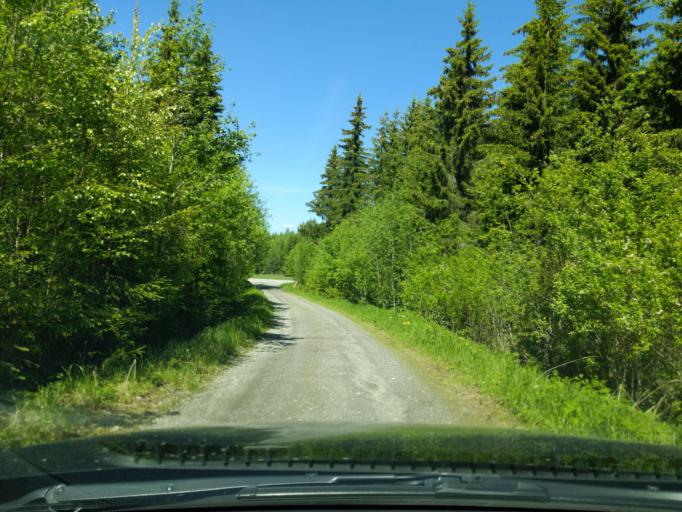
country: FI
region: Paijanne Tavastia
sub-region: Lahti
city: Lahti
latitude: 61.0615
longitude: 25.6955
